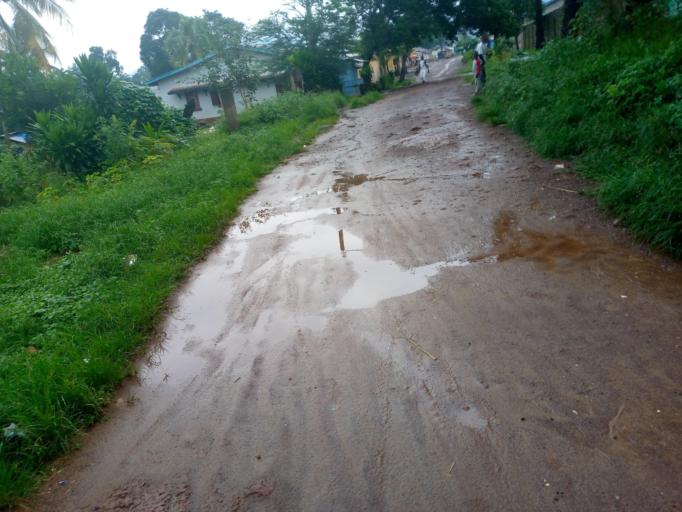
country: SL
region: Eastern Province
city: Kenema
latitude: 7.8828
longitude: -11.1799
